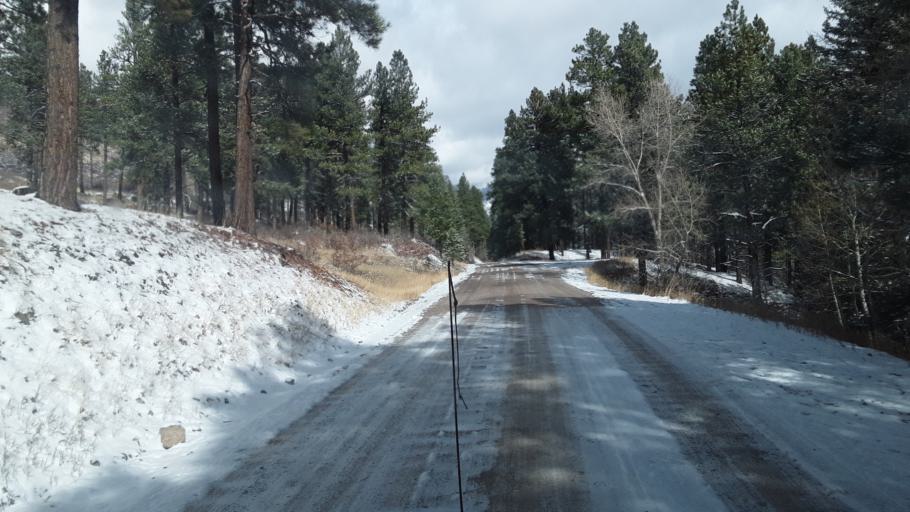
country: US
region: Colorado
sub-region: La Plata County
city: Bayfield
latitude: 37.4165
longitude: -107.5137
